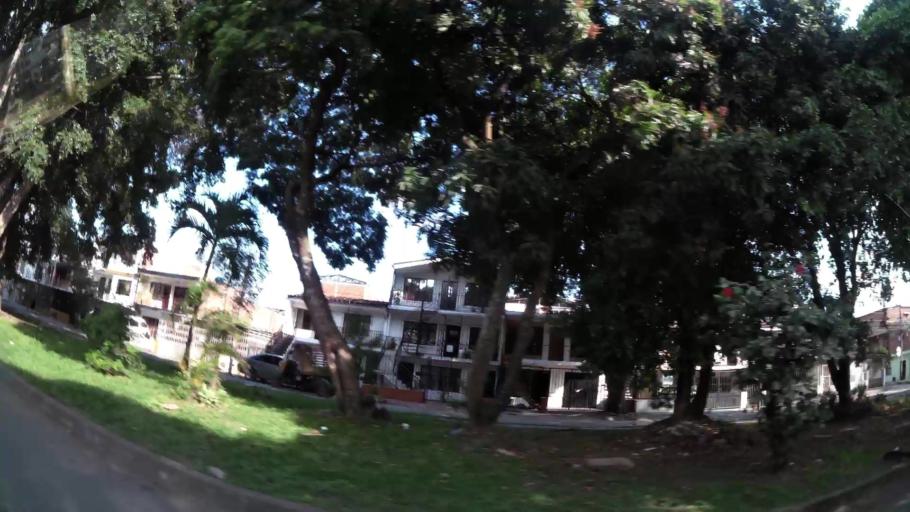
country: CO
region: Valle del Cauca
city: Cali
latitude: 3.4070
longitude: -76.5137
